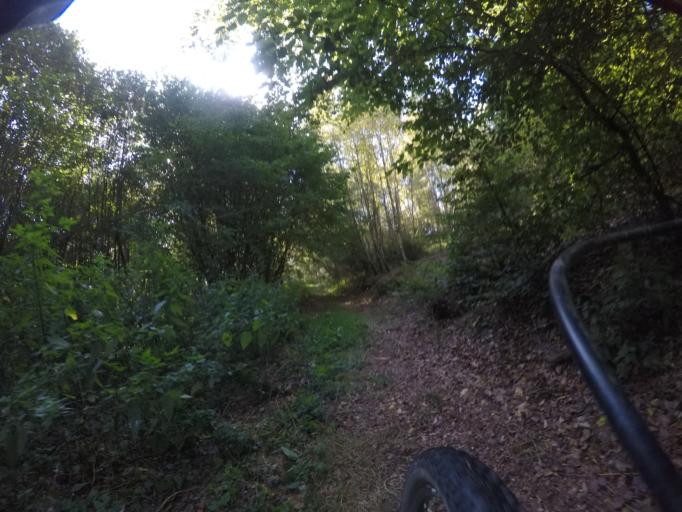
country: BE
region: Wallonia
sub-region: Province du Luxembourg
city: Fauvillers
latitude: 49.9030
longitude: 5.6744
